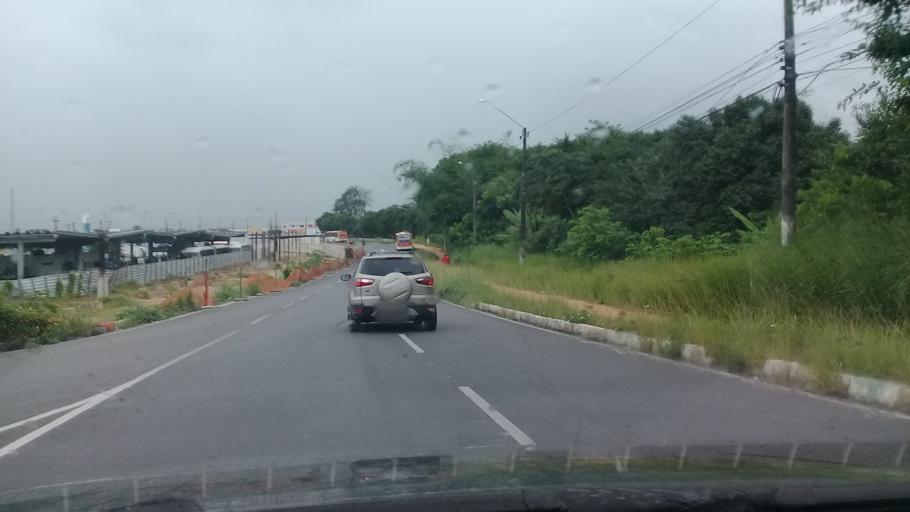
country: BR
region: Pernambuco
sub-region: Igarassu
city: Igarassu
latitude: -7.8339
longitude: -34.9121
